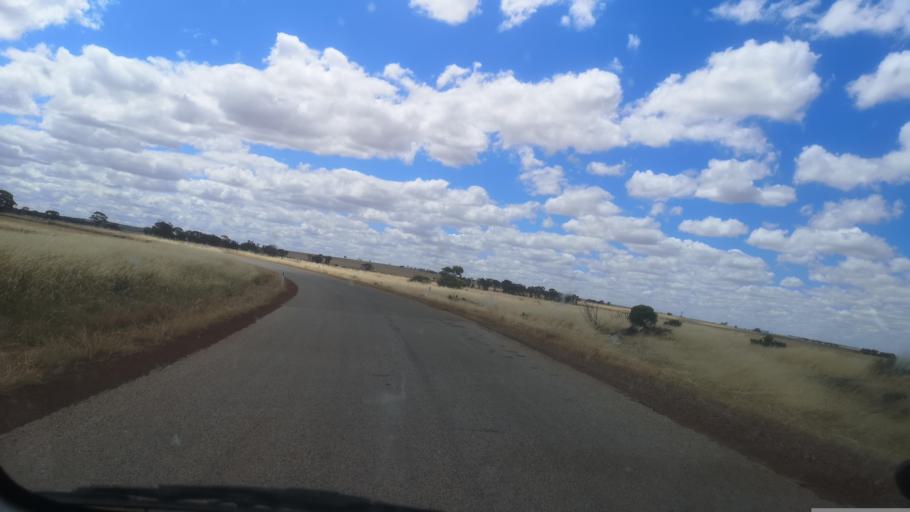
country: AU
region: Western Australia
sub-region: Cunderdin
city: Cunderdin
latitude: -32.0546
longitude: 117.4235
